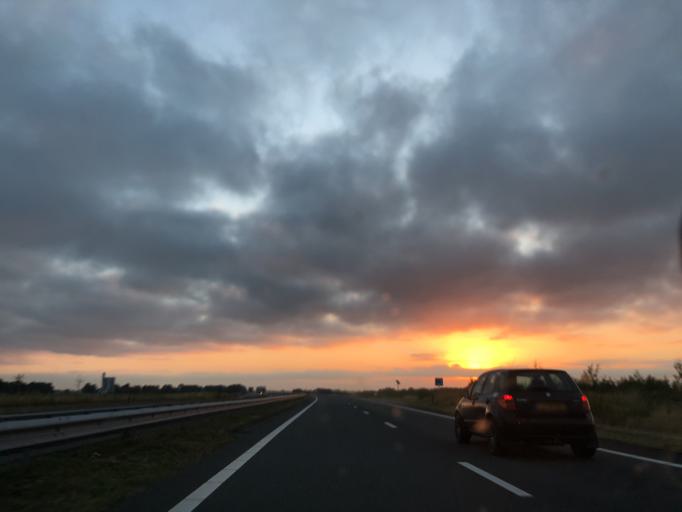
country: NL
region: Groningen
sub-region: Gemeente Veendam
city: Veendam
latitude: 53.0960
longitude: 6.8942
